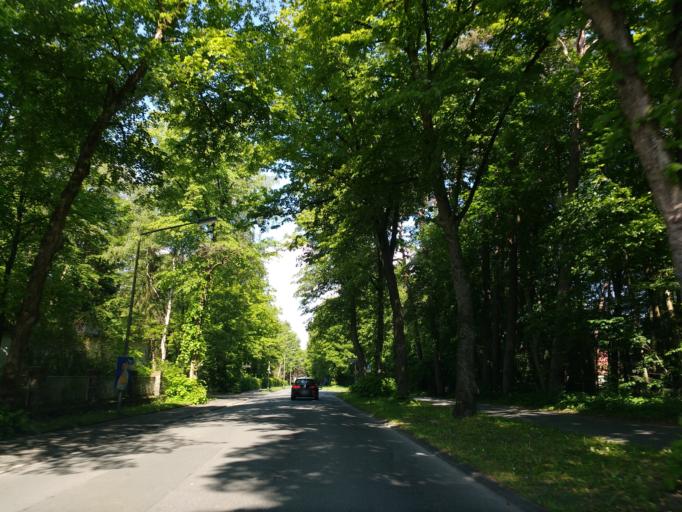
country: DE
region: North Rhine-Westphalia
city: Bad Lippspringe
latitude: 51.7858
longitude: 8.8052
